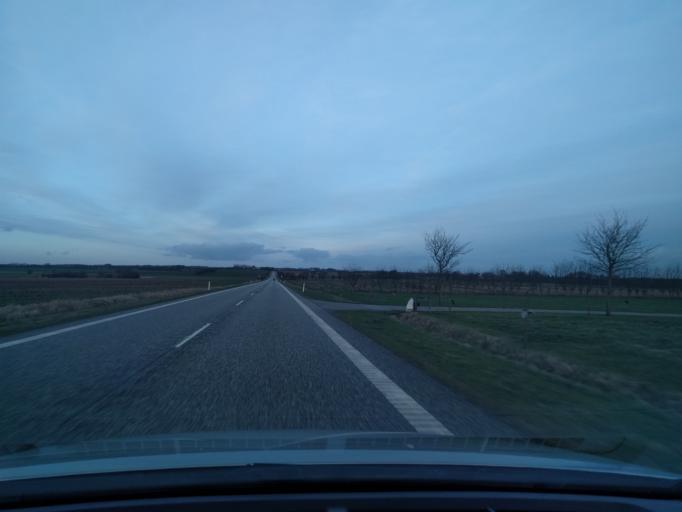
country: DK
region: South Denmark
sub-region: Tonder Kommune
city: Logumkloster
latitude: 55.1237
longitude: 8.9732
